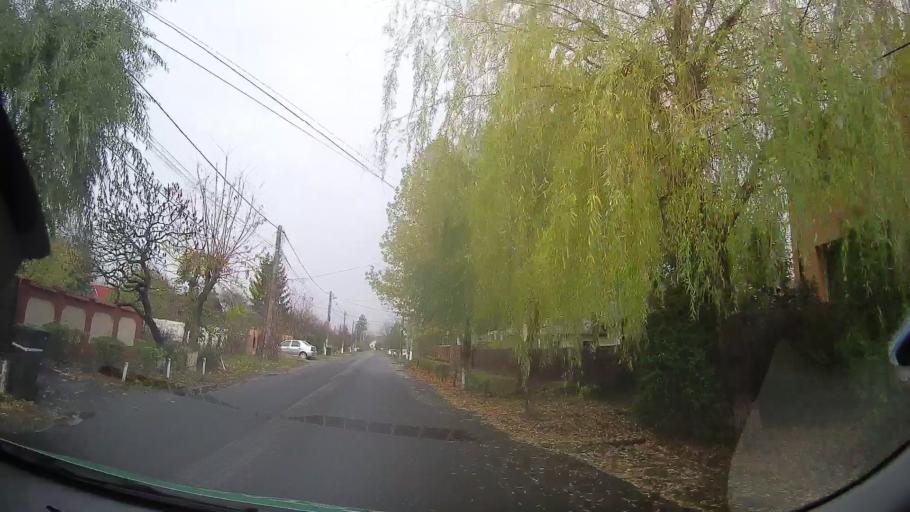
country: RO
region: Ilfov
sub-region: Comuna Snagov
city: Snagov
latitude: 44.7093
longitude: 26.1711
